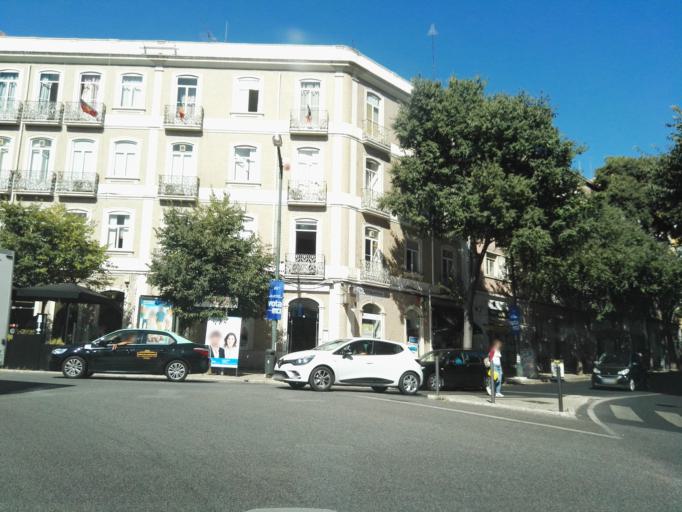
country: PT
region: Lisbon
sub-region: Lisbon
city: Lisbon
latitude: 38.7312
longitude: -9.1407
